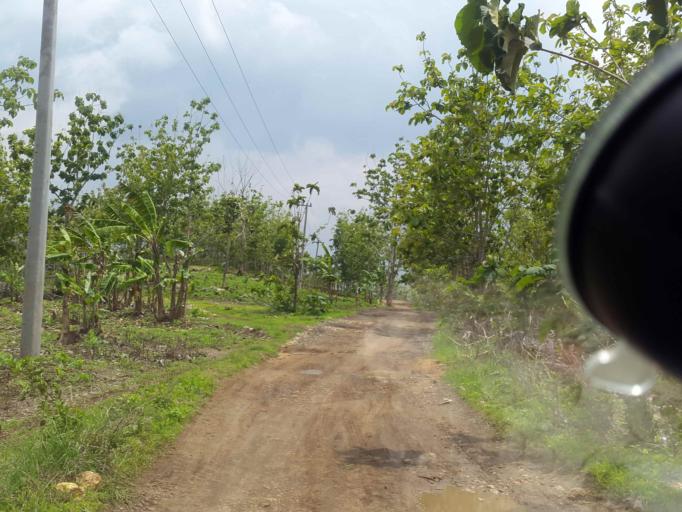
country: ID
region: East Java
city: Tumpakoyot
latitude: -8.2918
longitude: 112.0295
